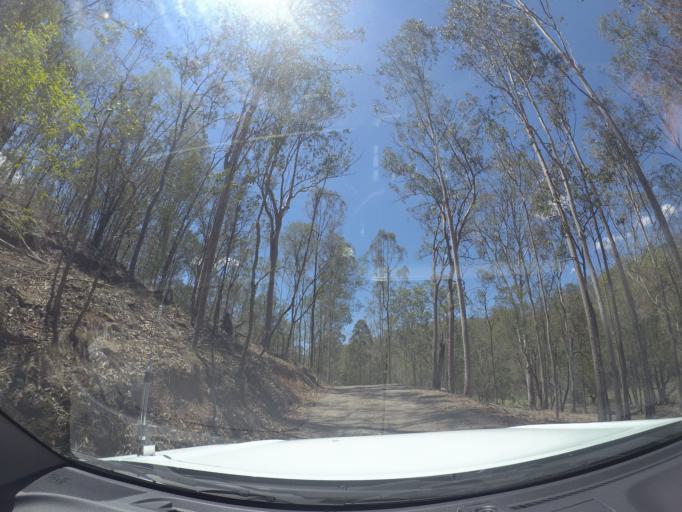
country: AU
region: Queensland
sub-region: Ipswich
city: Deebing Heights
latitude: -27.7614
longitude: 152.8084
